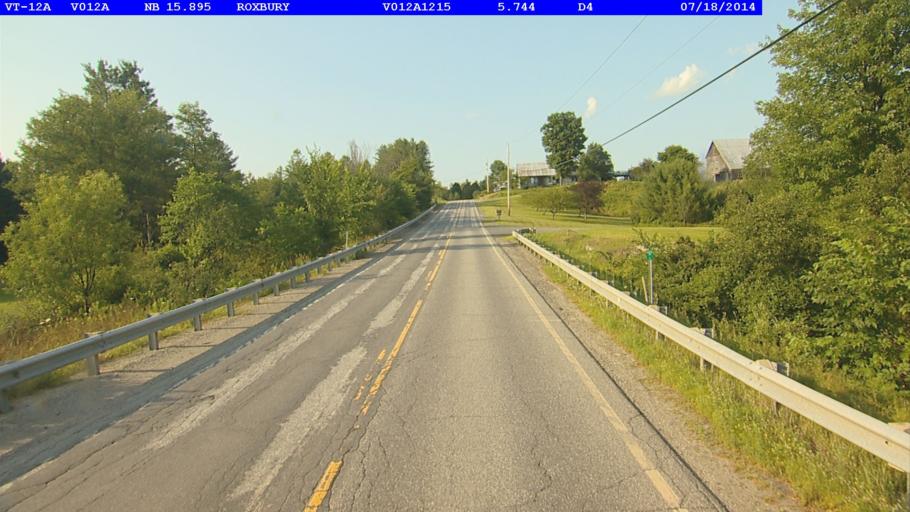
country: US
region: Vermont
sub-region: Washington County
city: Northfield
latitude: 44.1077
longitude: -72.7281
